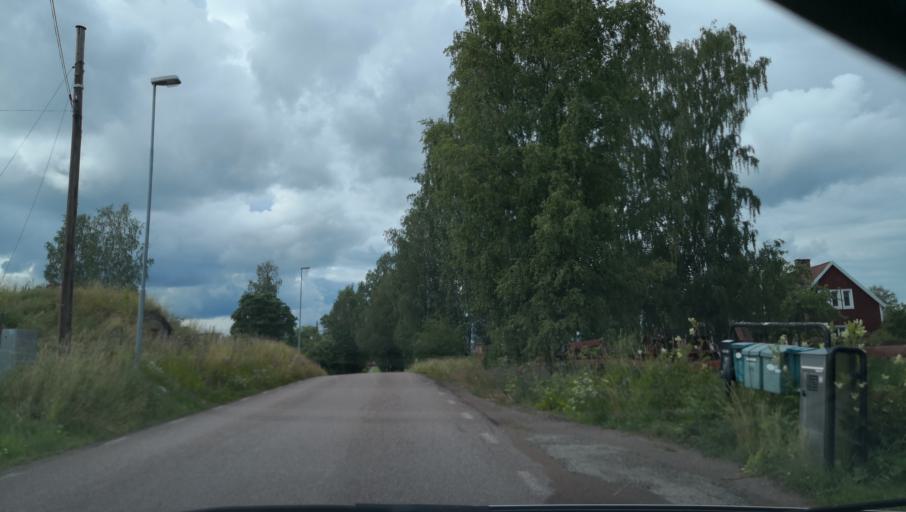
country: SE
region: Dalarna
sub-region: Borlange Kommun
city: Ornas
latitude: 60.4445
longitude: 15.5859
